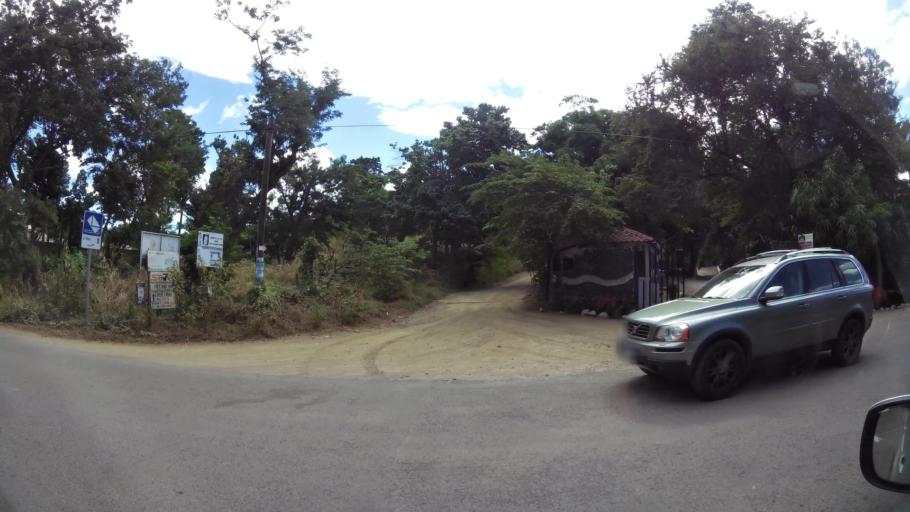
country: CR
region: Guanacaste
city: Santa Cruz
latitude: 10.3052
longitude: -85.8372
